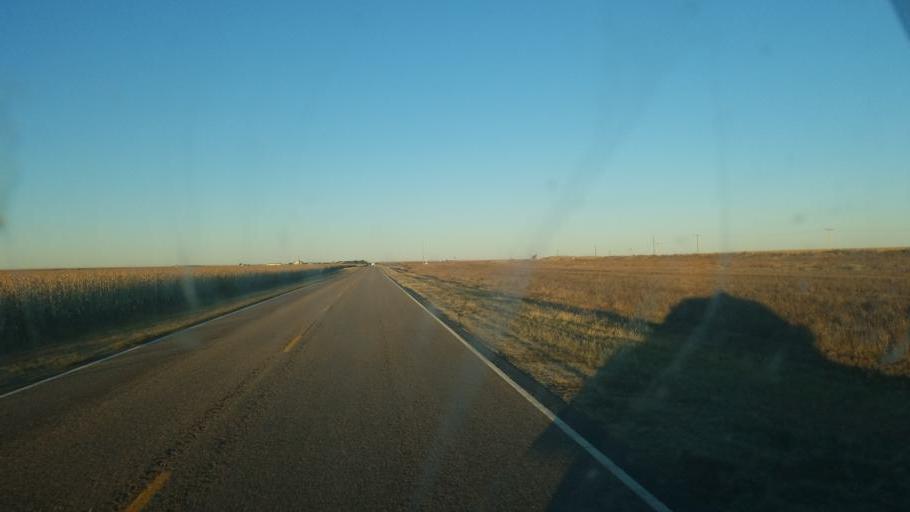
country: US
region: Colorado
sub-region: Cheyenne County
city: Cheyenne Wells
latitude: 38.8561
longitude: -102.0541
